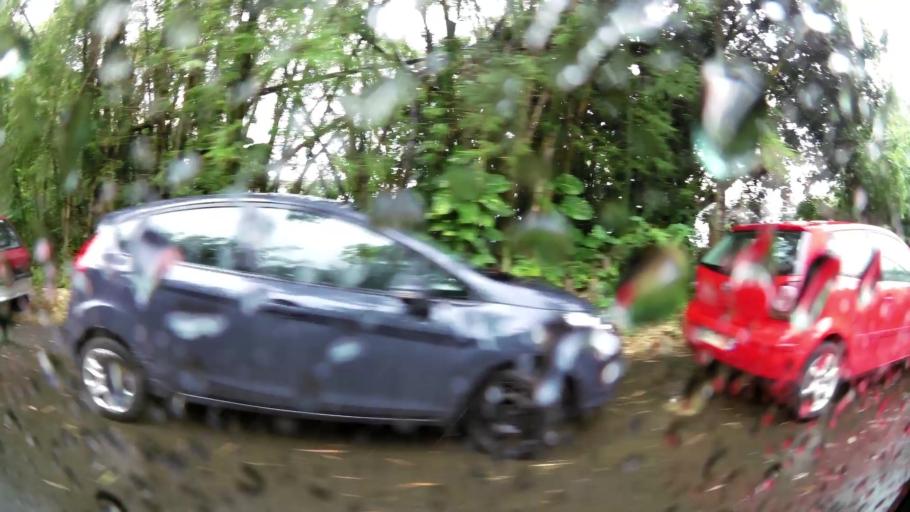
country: RE
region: Reunion
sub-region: Reunion
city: Saint-Andre
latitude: -20.9646
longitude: 55.6487
